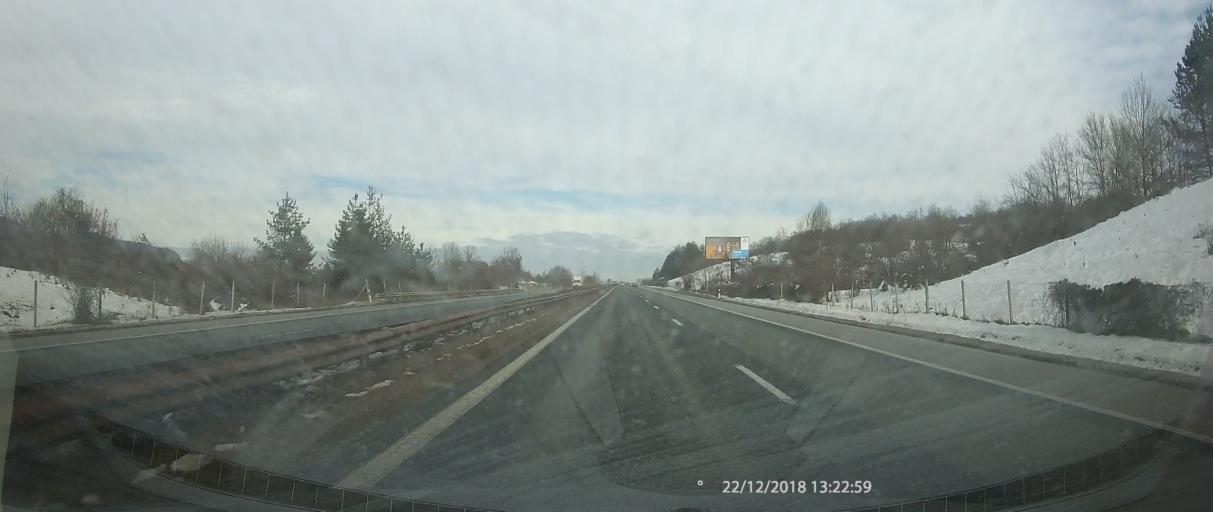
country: BG
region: Lovech
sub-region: Obshtina Yablanitsa
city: Yablanitsa
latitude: 42.9960
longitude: 24.0771
